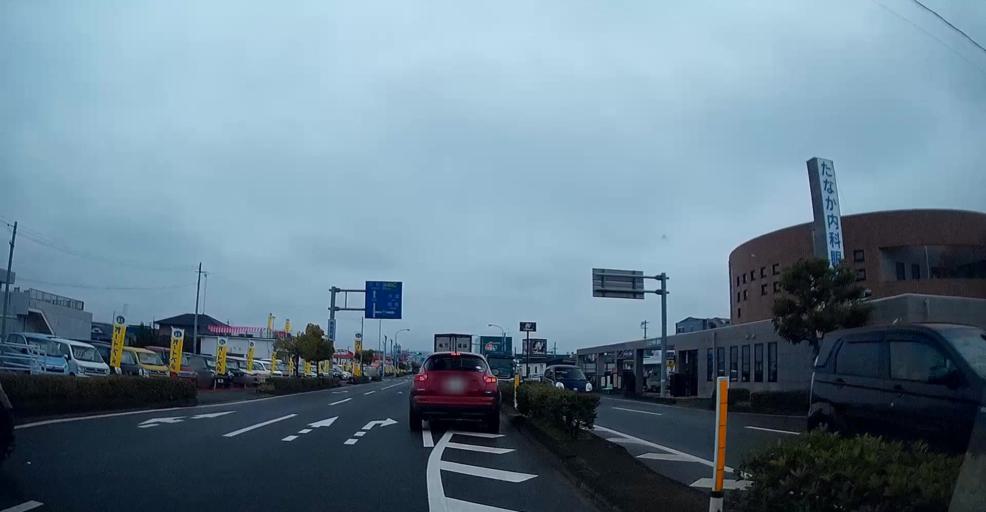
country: JP
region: Kumamoto
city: Kumamoto
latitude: 32.7498
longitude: 130.7394
